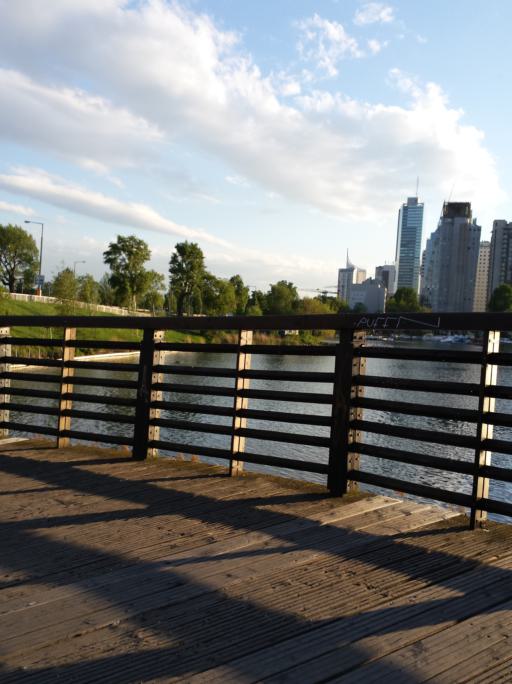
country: AT
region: Vienna
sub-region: Wien Stadt
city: Vienna
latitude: 48.2392
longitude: 16.4284
